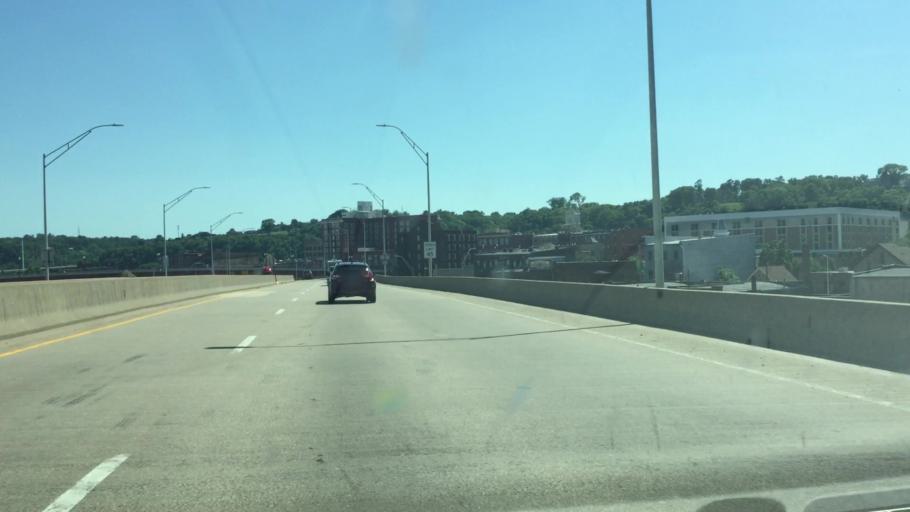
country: US
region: Iowa
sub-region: Dubuque County
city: Dubuque
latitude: 42.5003
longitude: -90.6621
